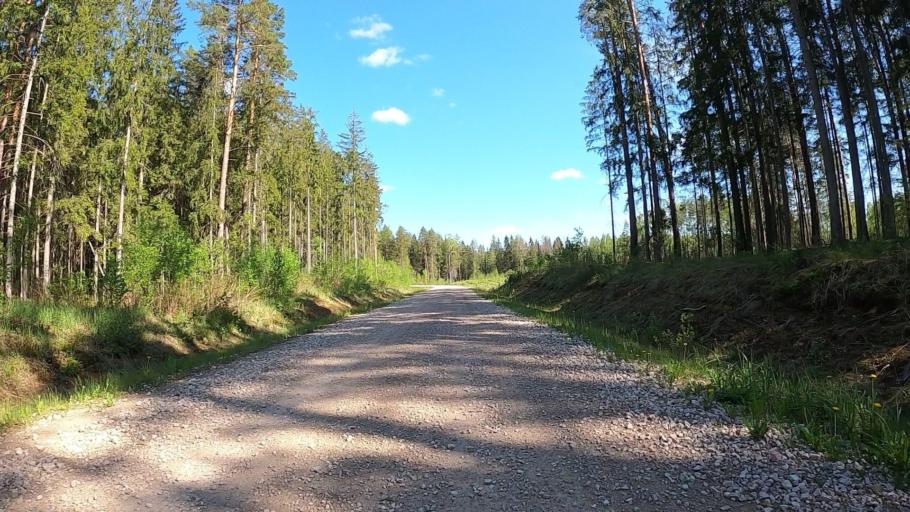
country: LV
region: Baldone
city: Baldone
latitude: 56.7830
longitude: 24.3474
